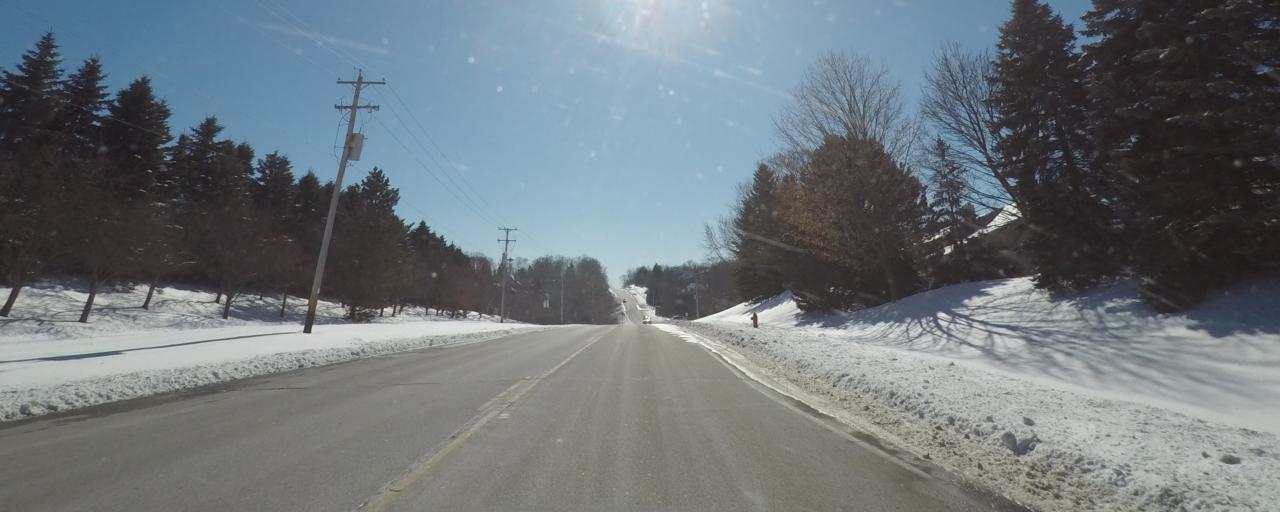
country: US
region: Wisconsin
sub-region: Waukesha County
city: Brookfield
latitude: 43.0257
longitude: -88.1468
